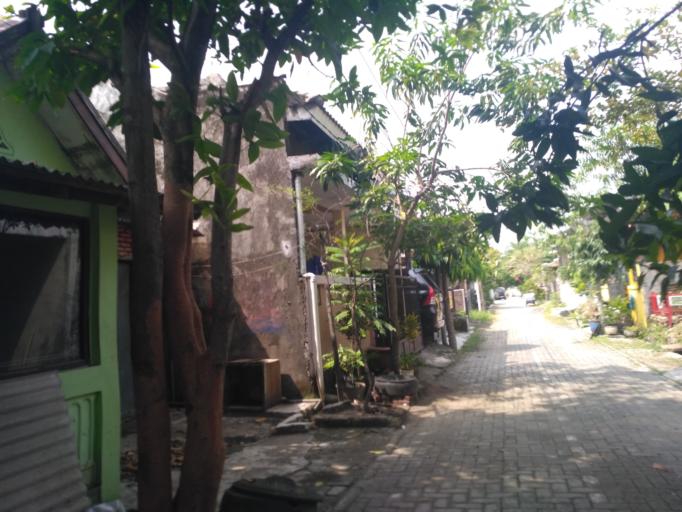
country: ID
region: Central Java
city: Mranggen
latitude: -7.0620
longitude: 110.4646
